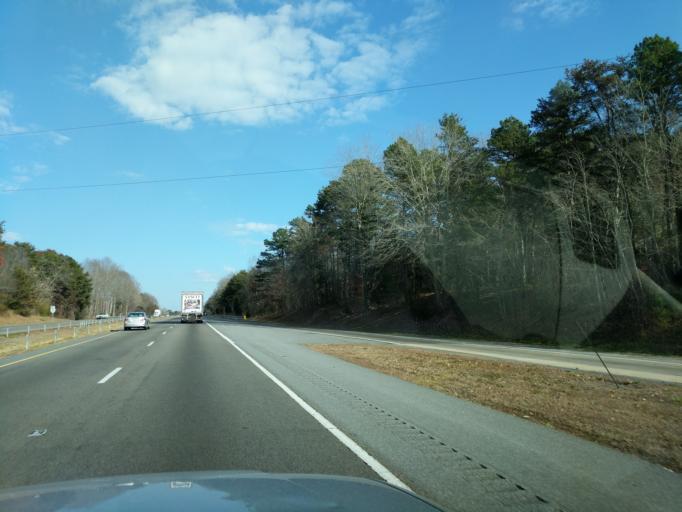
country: US
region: North Carolina
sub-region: Alexander County
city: Stony Point
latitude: 35.7642
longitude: -81.0212
